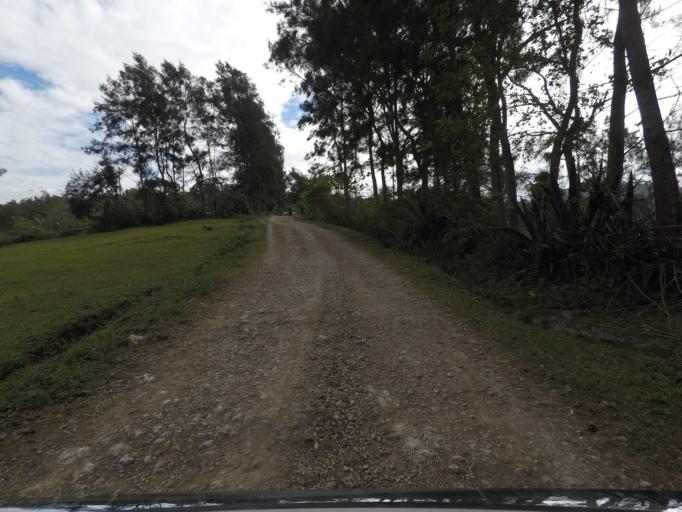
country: TL
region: Baucau
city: Venilale
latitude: -8.6521
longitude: 126.3920
